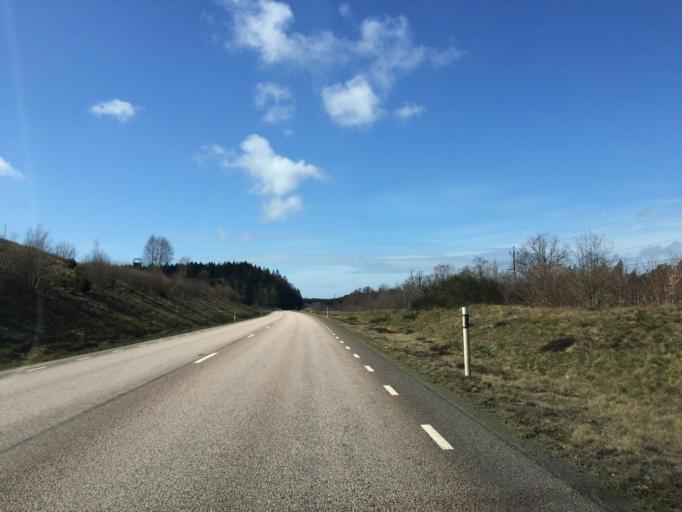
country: SE
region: Halland
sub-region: Laholms Kommun
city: Knared
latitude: 56.5193
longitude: 13.2831
